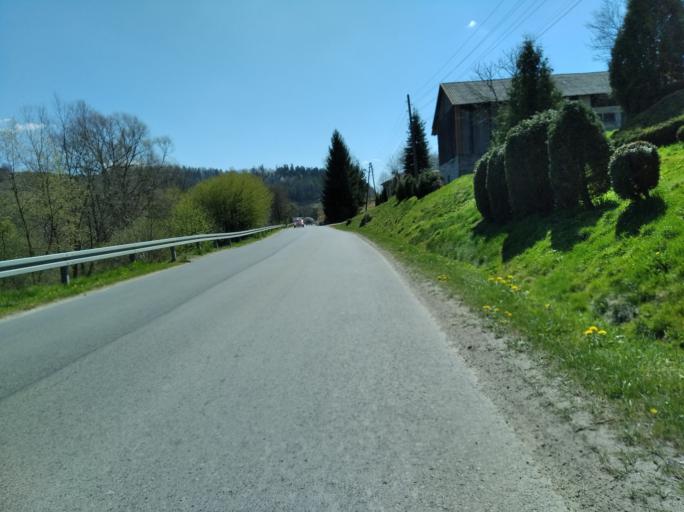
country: PL
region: Subcarpathian Voivodeship
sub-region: Powiat brzozowski
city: Dydnia
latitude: 49.6908
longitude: 22.1843
